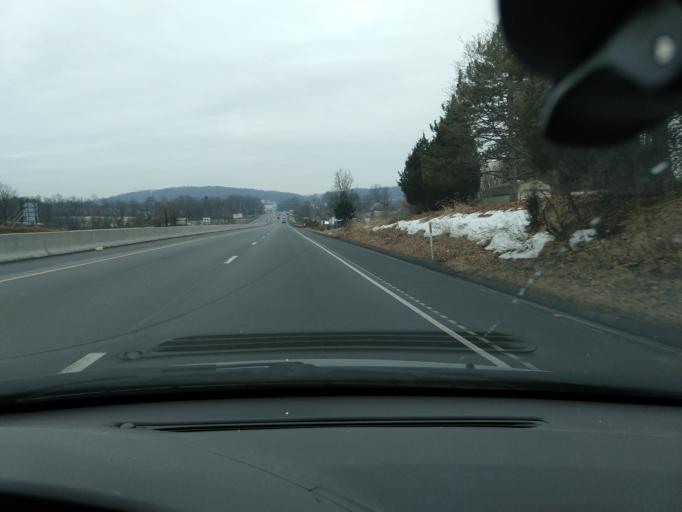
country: US
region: Pennsylvania
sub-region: Montgomery County
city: Gilbertsville
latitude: 40.3180
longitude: -75.6281
